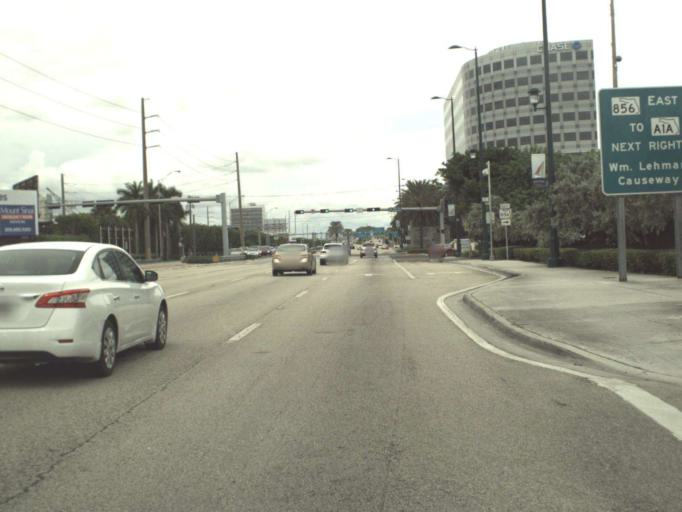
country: US
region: Florida
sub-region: Miami-Dade County
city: Ojus
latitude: 25.9540
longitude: -80.1466
